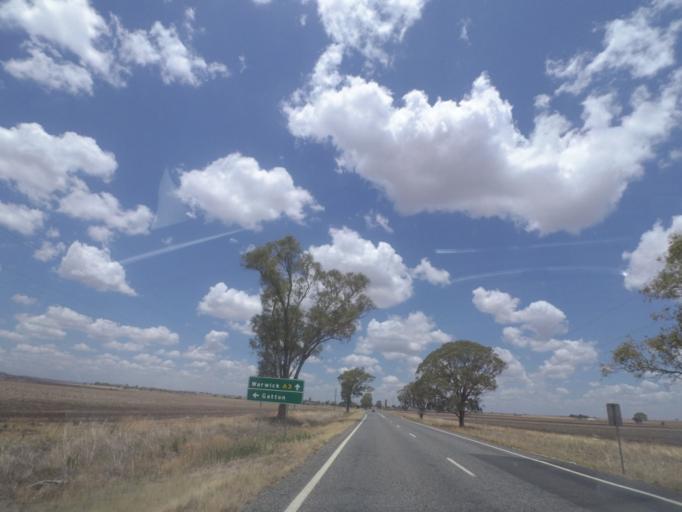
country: AU
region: Queensland
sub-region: Toowoomba
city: Top Camp
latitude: -27.9199
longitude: 151.9825
